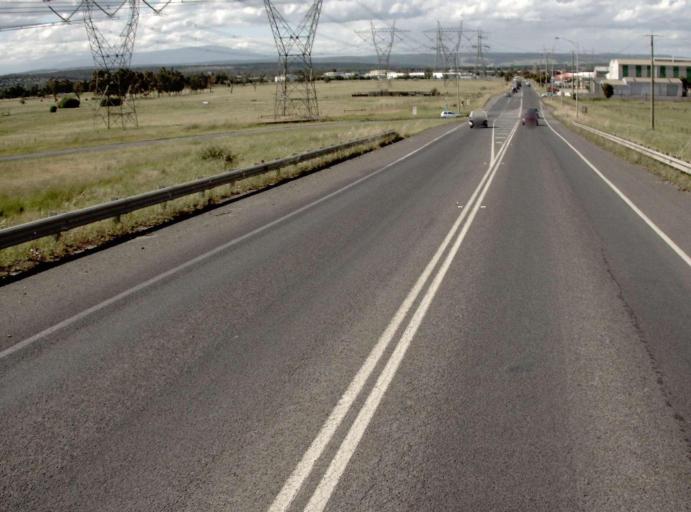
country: AU
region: Victoria
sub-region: Latrobe
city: Morwell
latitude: -38.2442
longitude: 146.4370
